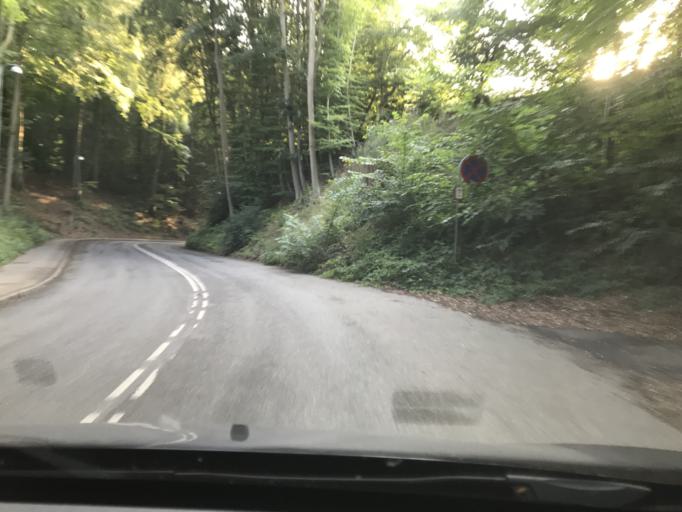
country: DK
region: South Denmark
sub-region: Vejle Kommune
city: Vejle
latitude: 55.7146
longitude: 9.5544
